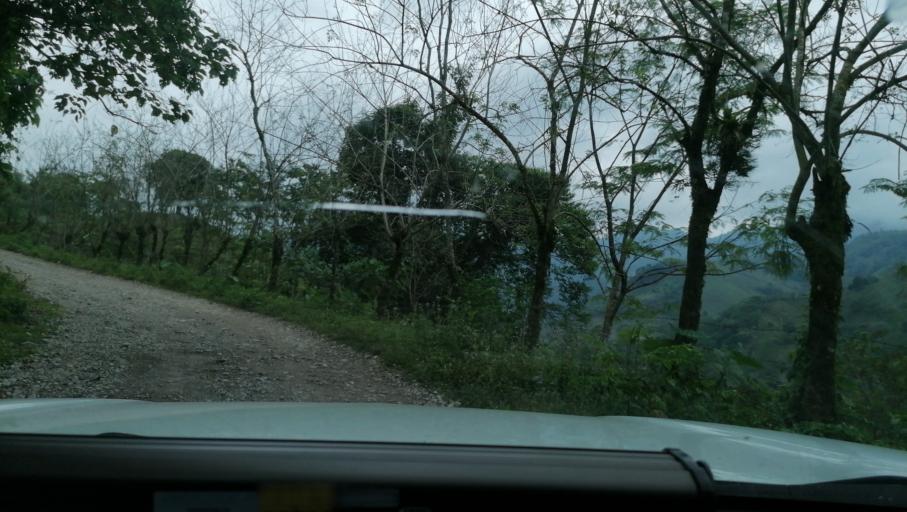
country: MX
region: Chiapas
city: Ocotepec
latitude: 17.3197
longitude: -93.1363
